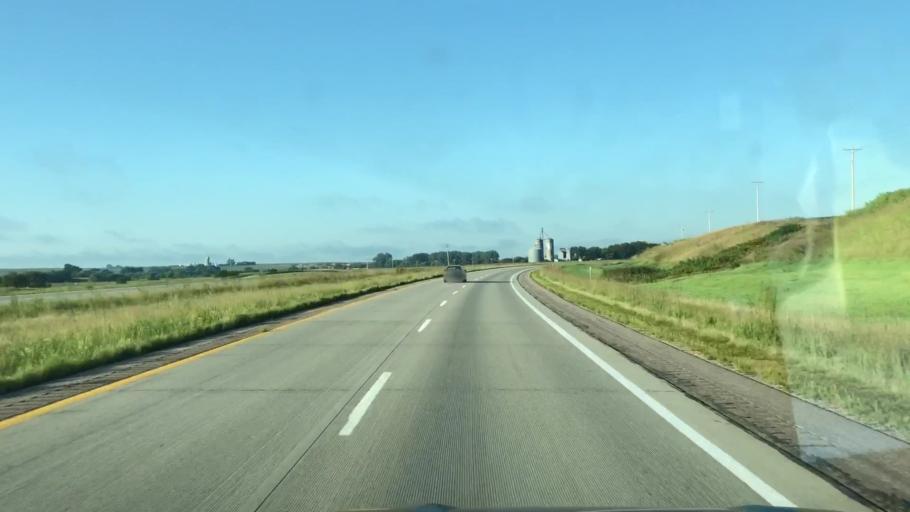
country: US
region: Iowa
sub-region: Sioux County
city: Alton
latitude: 42.9358
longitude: -96.0466
